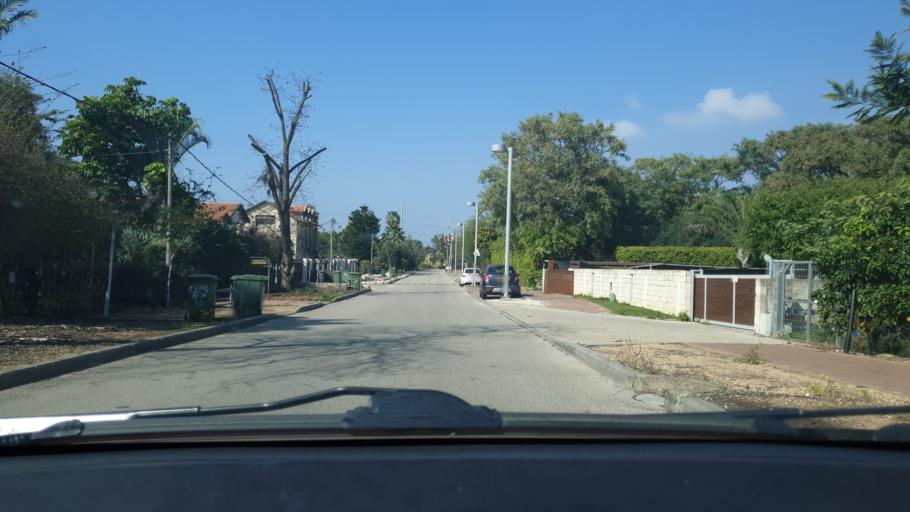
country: IL
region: Central District
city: Bet Dagan
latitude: 32.0079
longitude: 34.8198
